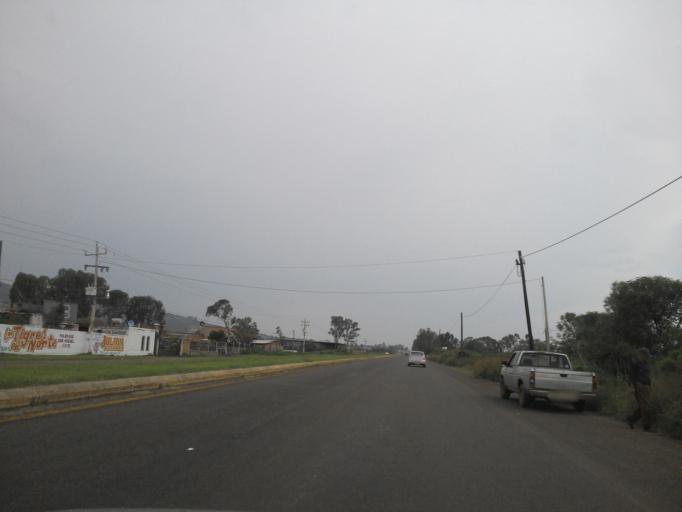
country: MX
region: Jalisco
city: Capilla de Guadalupe
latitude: 20.7619
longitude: -102.5464
